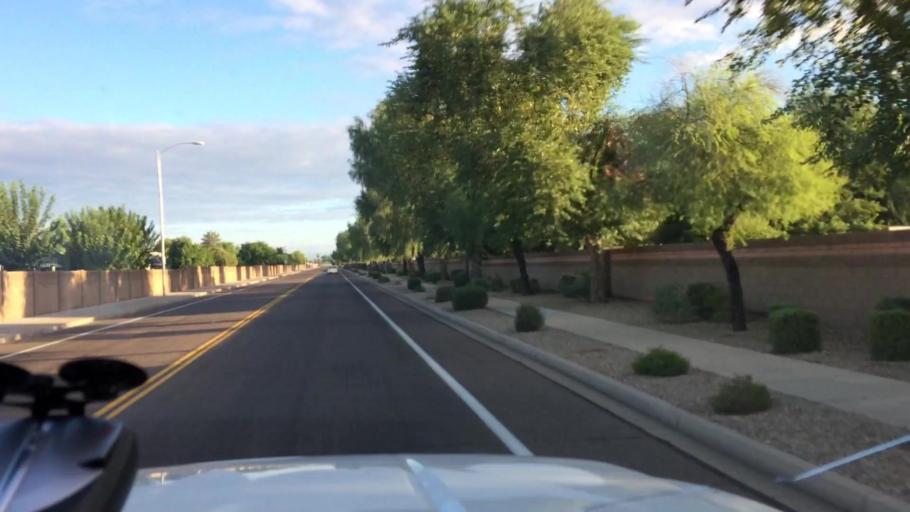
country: US
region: Arizona
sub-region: Maricopa County
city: Sun City
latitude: 33.5739
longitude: -112.2638
